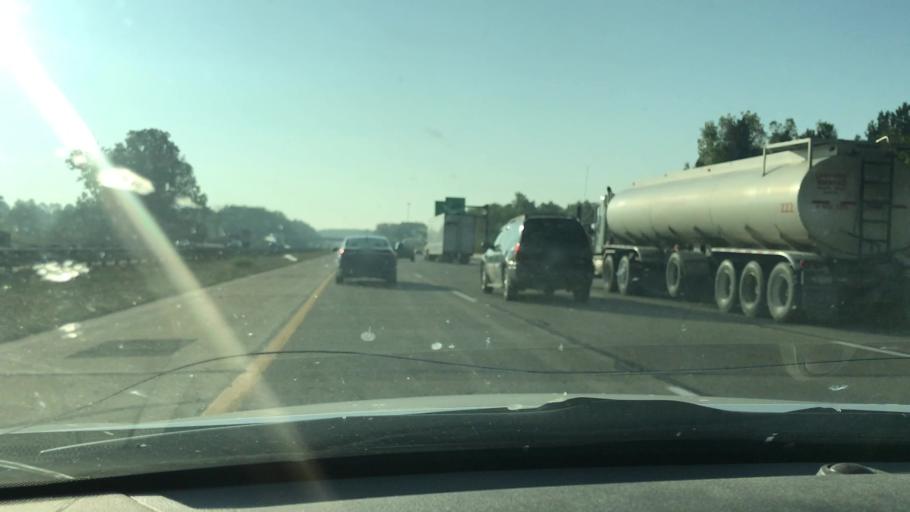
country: US
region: Michigan
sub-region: Livingston County
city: Howell
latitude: 42.5947
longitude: -83.9397
